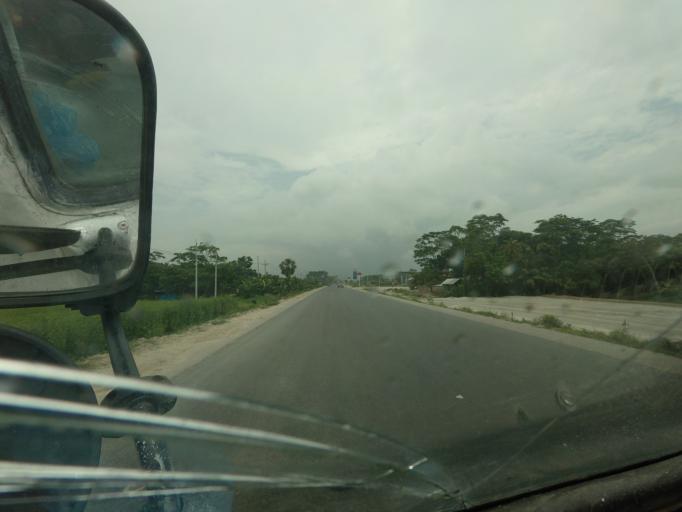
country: BD
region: Dhaka
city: Char Bhadrasan
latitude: 23.3749
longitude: 90.0242
